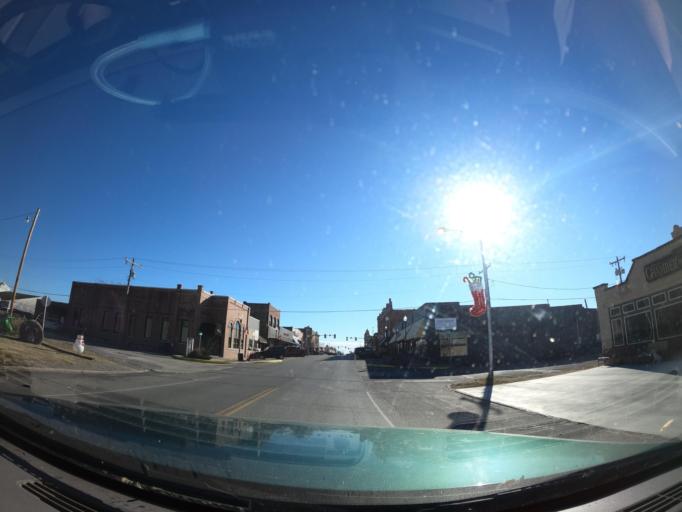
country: US
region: Oklahoma
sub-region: McIntosh County
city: Eufaula
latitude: 35.2884
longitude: -95.5824
